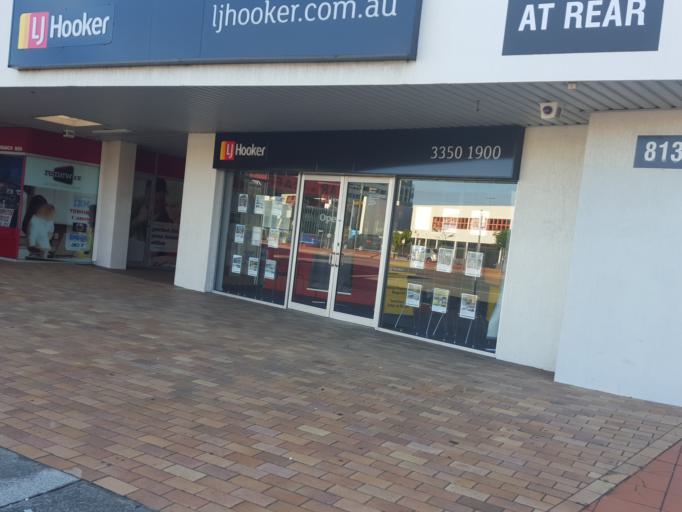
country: AU
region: Queensland
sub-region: Brisbane
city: Chermside West
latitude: -27.3875
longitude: 153.0313
